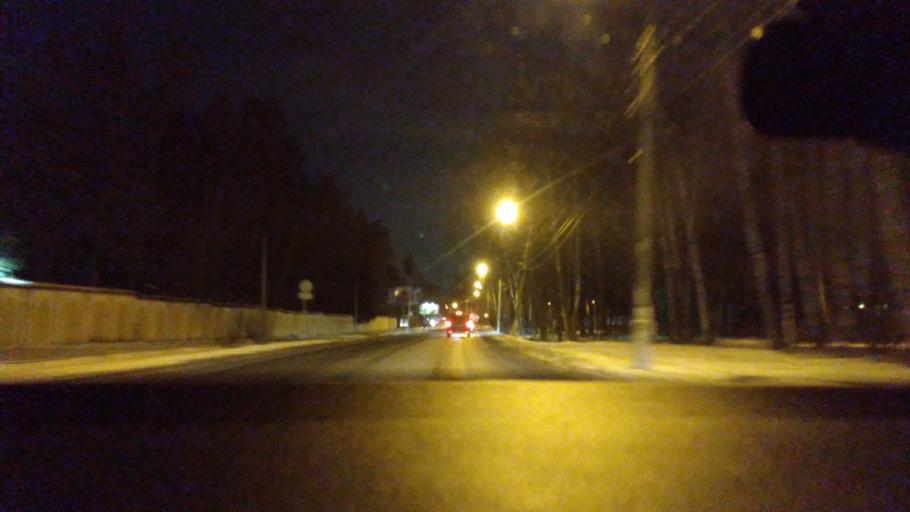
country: RU
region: Moskovskaya
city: Saltykovka
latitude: 55.7735
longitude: 37.9280
